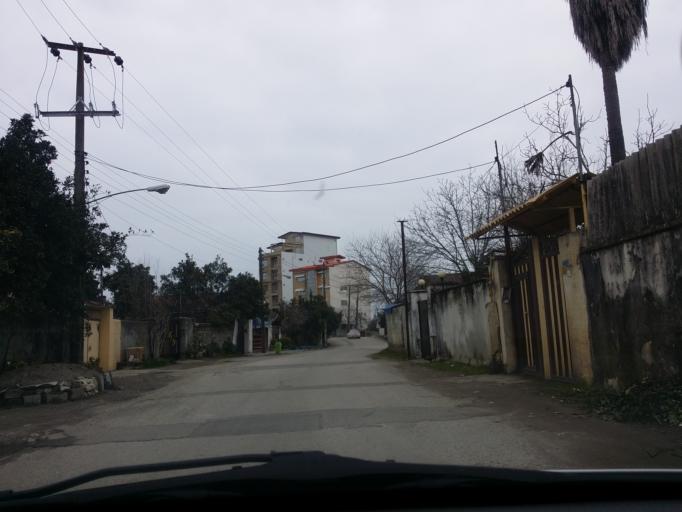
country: IR
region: Mazandaran
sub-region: Nowshahr
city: Nowshahr
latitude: 36.6543
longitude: 51.4769
